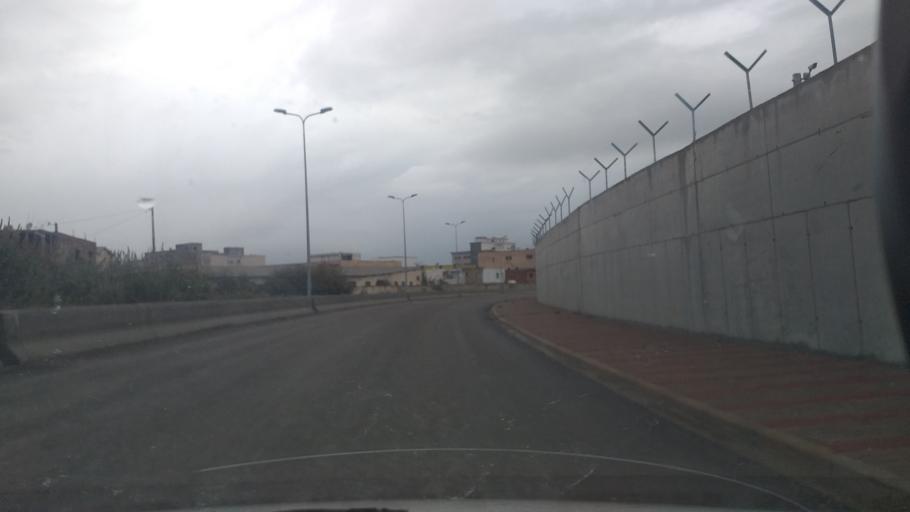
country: TN
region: Ariana
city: Ariana
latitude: 36.8596
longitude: 10.2144
